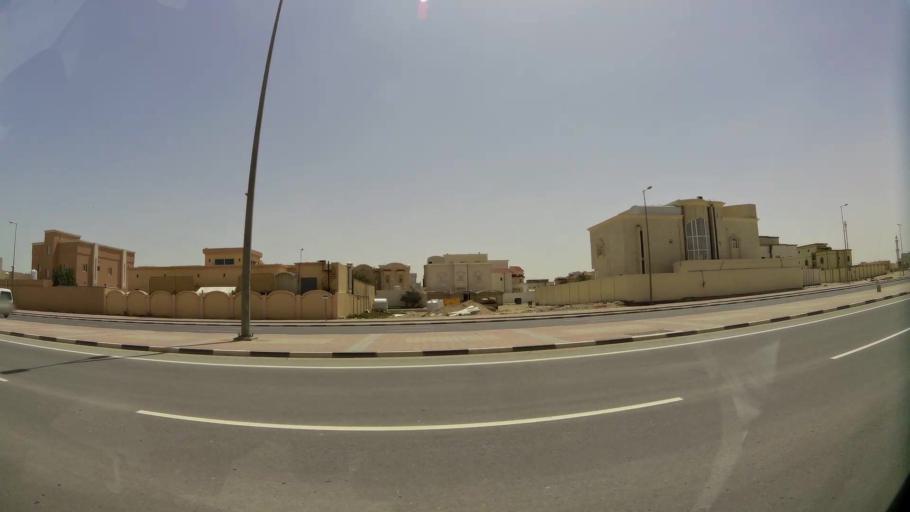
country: QA
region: Baladiyat Umm Salal
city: Umm Salal Muhammad
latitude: 25.4093
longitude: 51.4461
